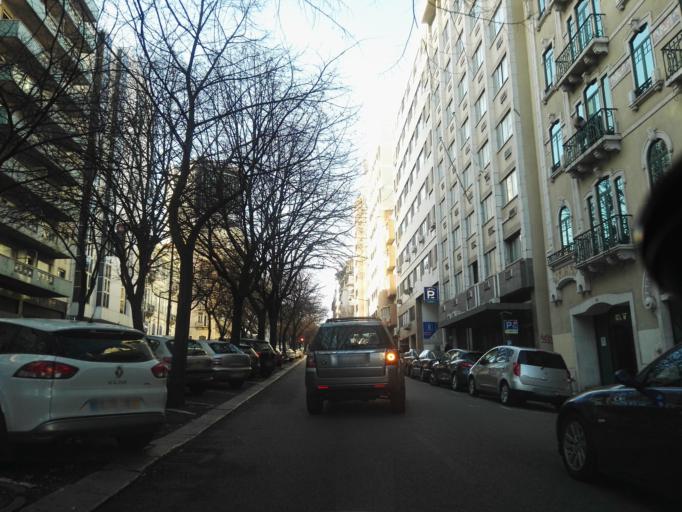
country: PT
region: Lisbon
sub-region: Lisbon
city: Lisbon
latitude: 38.7319
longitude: -9.1416
